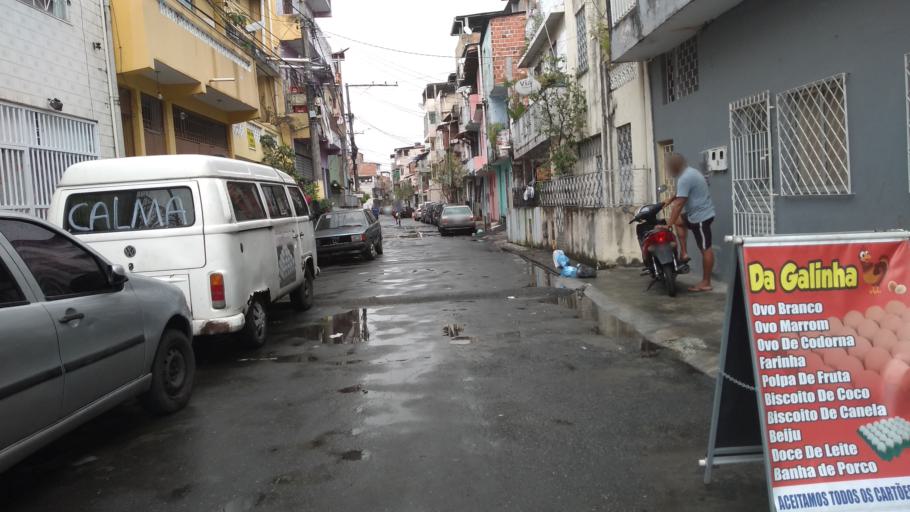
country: BR
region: Bahia
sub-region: Salvador
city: Salvador
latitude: -12.9184
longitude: -38.4990
